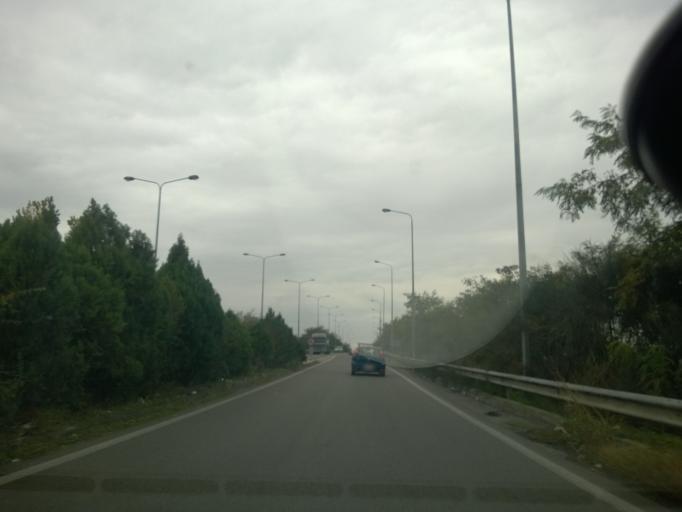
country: GR
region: Central Macedonia
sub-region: Nomos Pellis
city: Melissi
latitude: 40.7778
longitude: 22.3628
